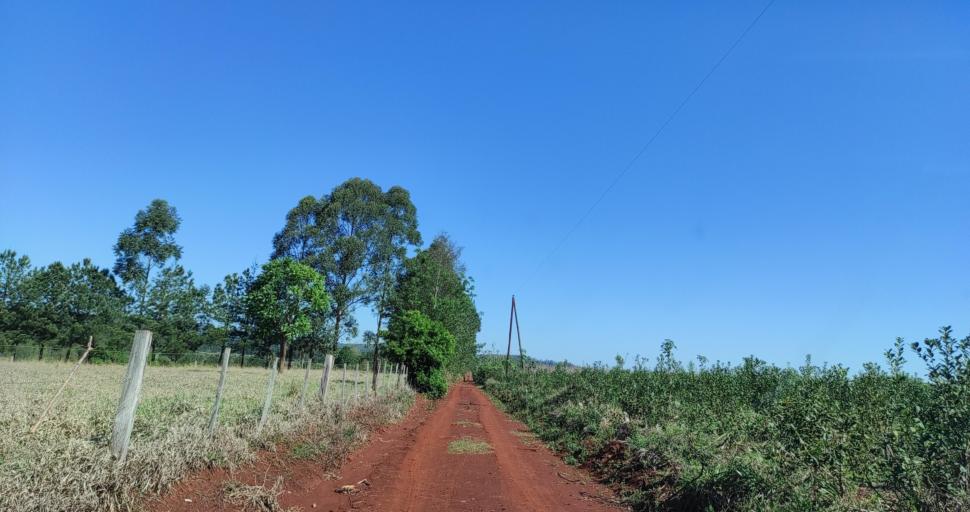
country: AR
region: Misiones
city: Capiovi
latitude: -26.9113
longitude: -55.0197
